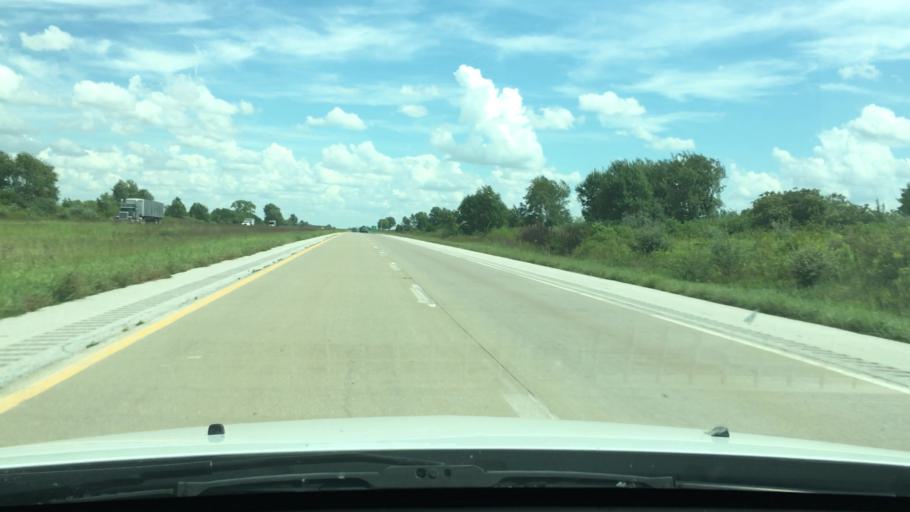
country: US
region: Illinois
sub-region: Scott County
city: Winchester
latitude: 39.6810
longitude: -90.4904
